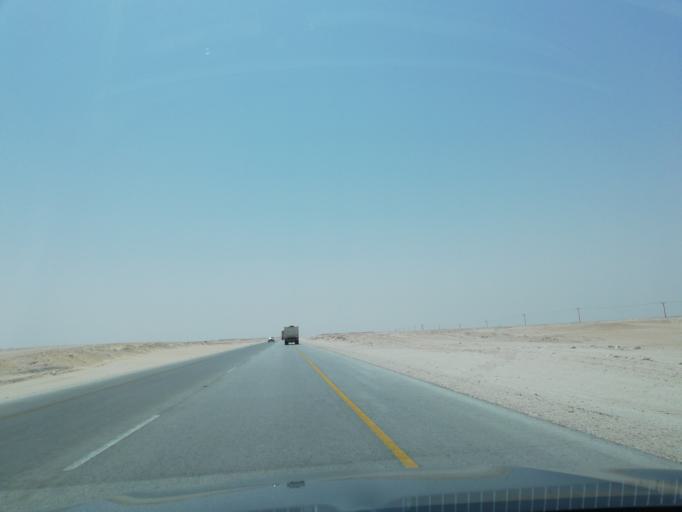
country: OM
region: Al Wusta
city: Hayma'
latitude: 19.6074
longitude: 55.6617
